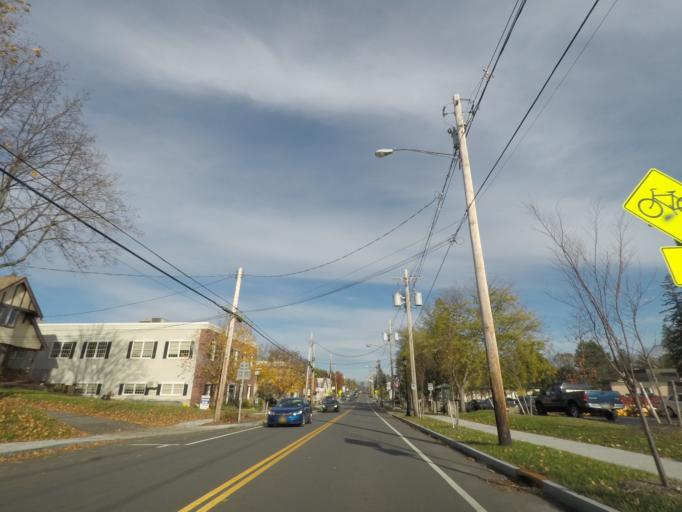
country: US
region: New York
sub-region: Albany County
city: Delmar
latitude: 42.6225
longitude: -73.8320
